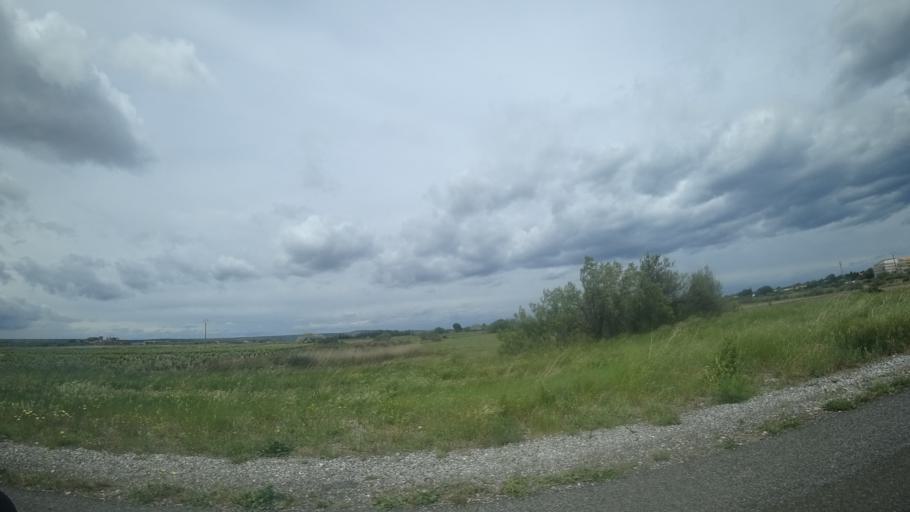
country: FR
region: Languedoc-Roussillon
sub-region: Departement de l'Aude
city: Leucate
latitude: 42.9325
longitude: 3.0077
